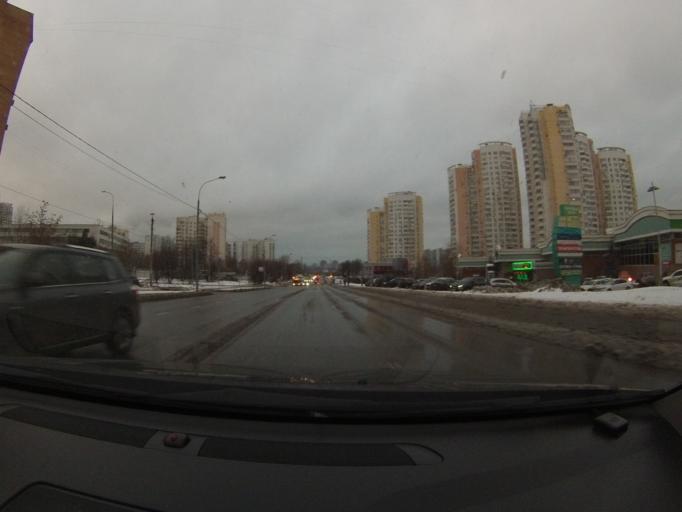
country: RU
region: Moscow
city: Nikol'skoye
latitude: 55.6828
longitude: 37.4905
